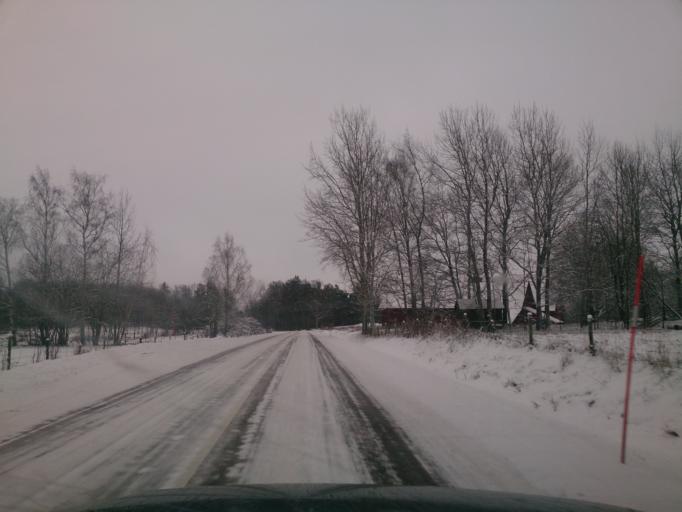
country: SE
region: OEstergoetland
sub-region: Norrkopings Kommun
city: Kimstad
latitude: 58.4279
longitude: 15.9056
